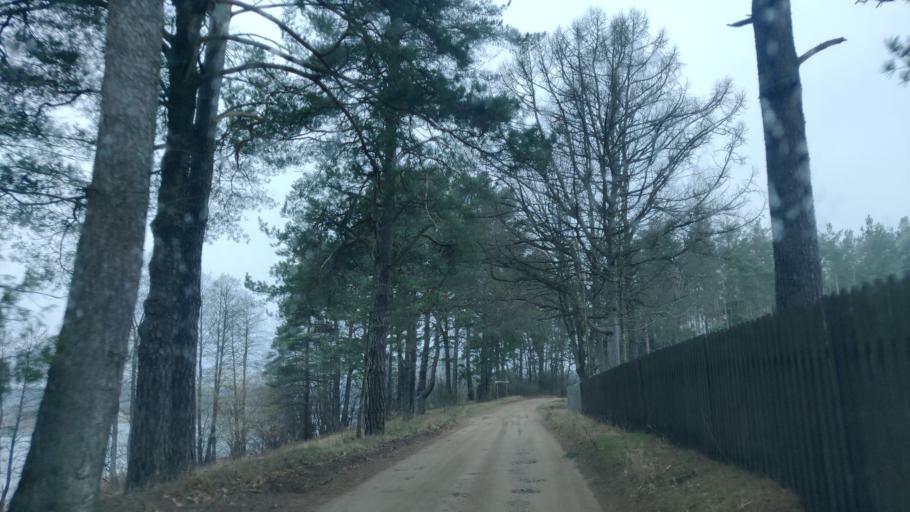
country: LT
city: Trakai
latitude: 54.5521
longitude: 24.9446
